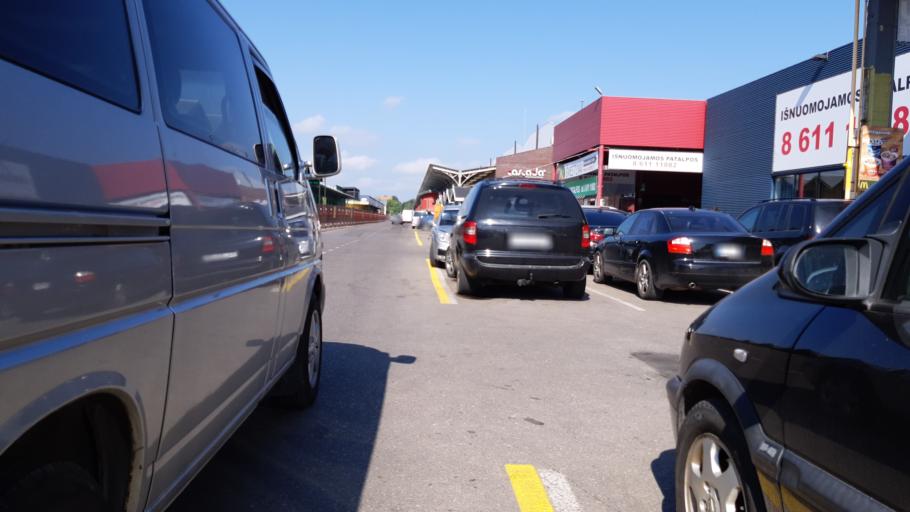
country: LT
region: Kauno apskritis
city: Dainava (Kaunas)
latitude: 54.9156
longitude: 23.9929
